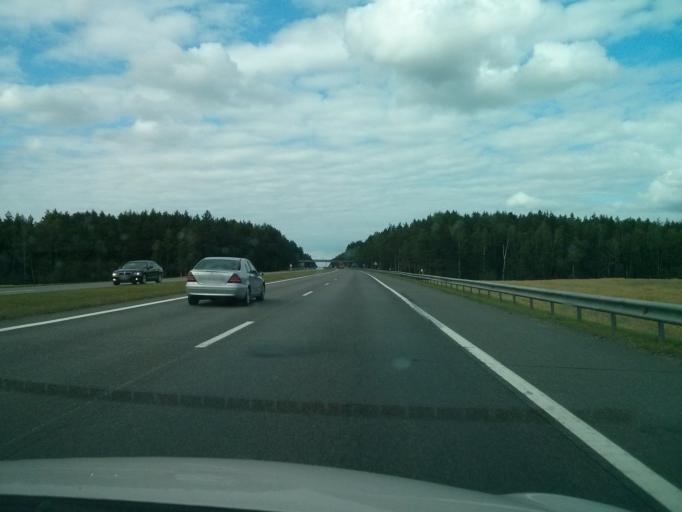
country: BY
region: Minsk
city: Zamostochcha
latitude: 53.8875
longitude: 27.9396
